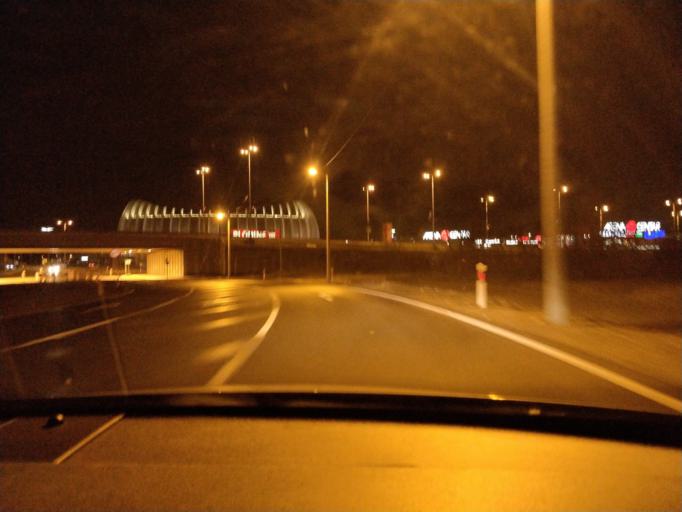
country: HR
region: Grad Zagreb
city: Novi Zagreb
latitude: 45.7749
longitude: 15.9425
